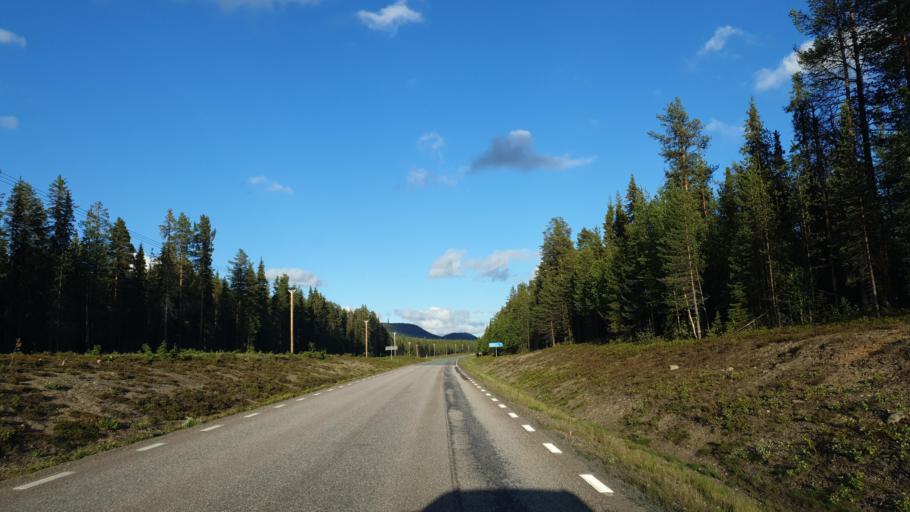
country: SE
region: Norrbotten
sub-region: Arvidsjaurs Kommun
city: Arvidsjaur
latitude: 65.7270
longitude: 18.6696
